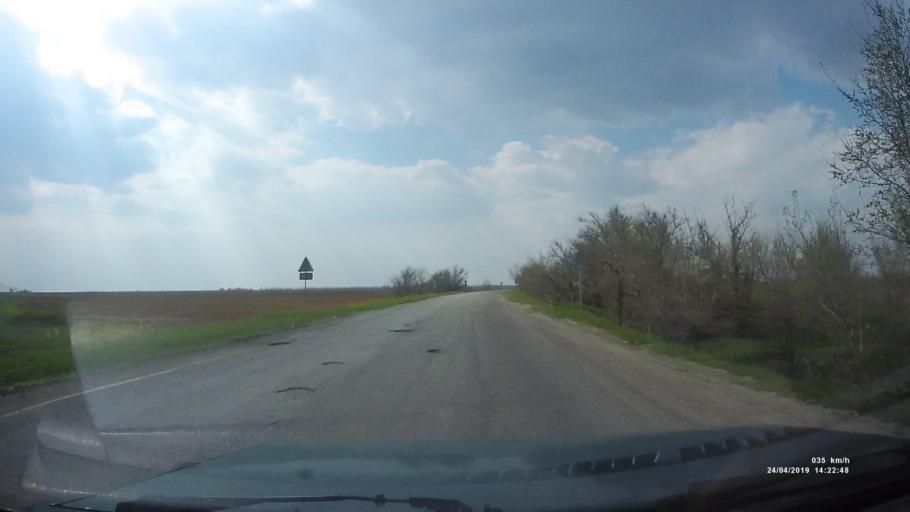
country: RU
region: Kalmykiya
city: Arshan'
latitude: 46.3178
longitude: 44.1216
